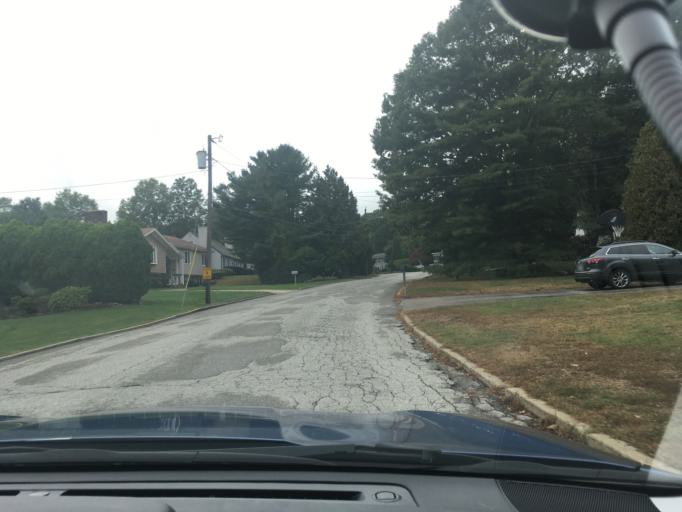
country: US
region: Rhode Island
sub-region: Kent County
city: East Greenwich
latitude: 41.6363
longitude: -71.4712
